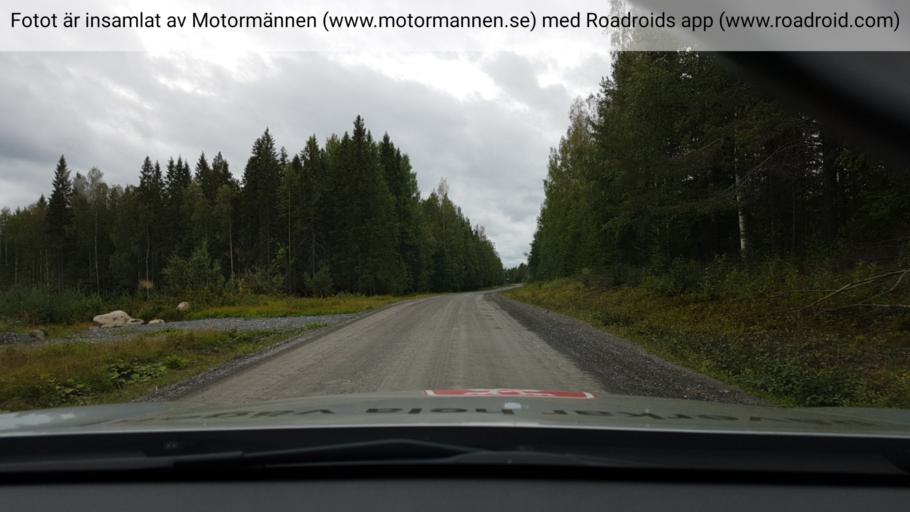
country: SE
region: Vaesterbotten
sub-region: Skelleftea Kommun
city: Forsbacka
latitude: 64.8318
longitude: 20.5014
